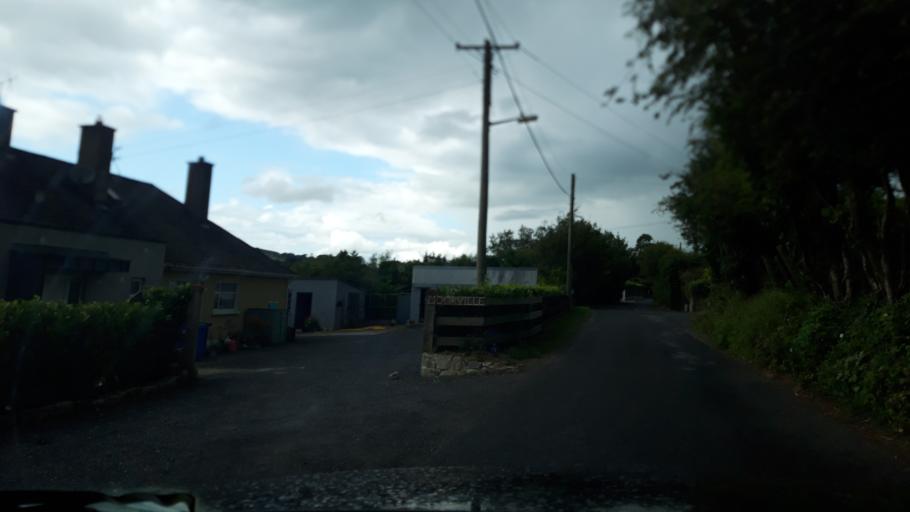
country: IE
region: Leinster
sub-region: Wicklow
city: Baltinglass
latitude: 52.9447
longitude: -6.7065
